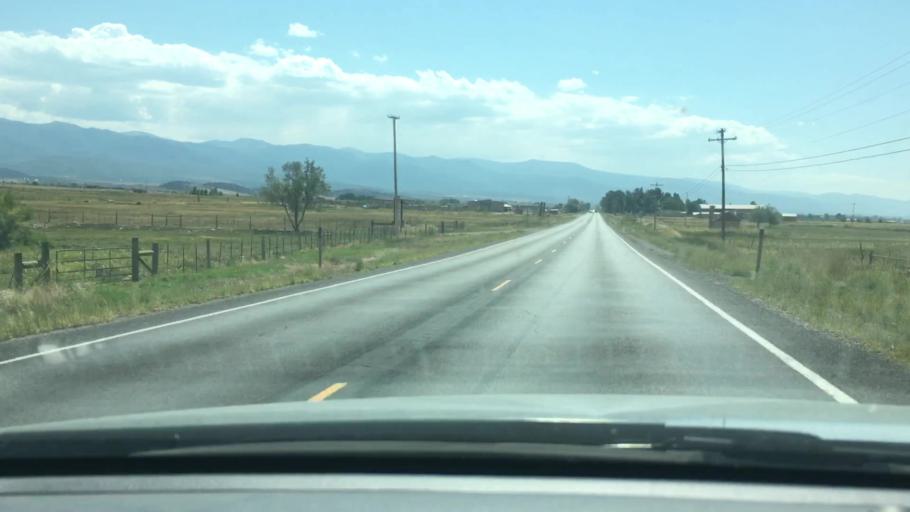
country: US
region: Utah
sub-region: Sanpete County
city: Fairview
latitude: 39.6116
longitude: -111.4449
